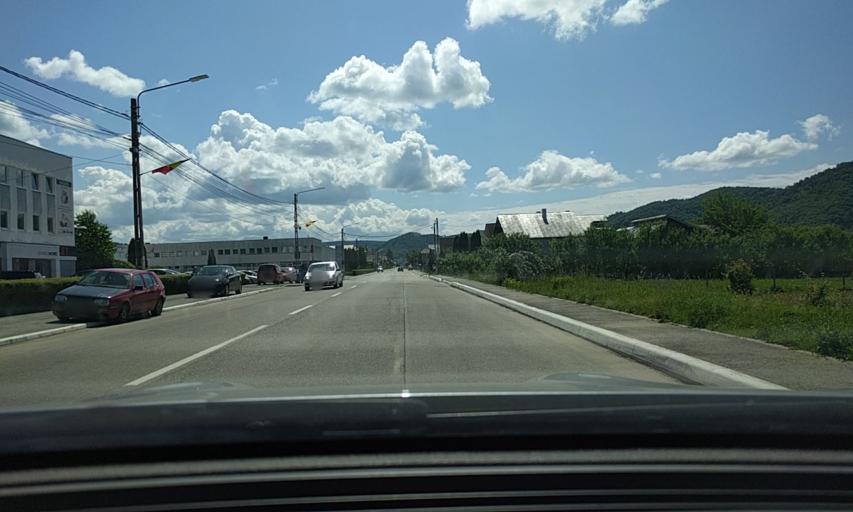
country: RO
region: Bistrita-Nasaud
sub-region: Oras Nasaud
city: Nasaud
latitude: 47.2960
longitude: 24.3814
